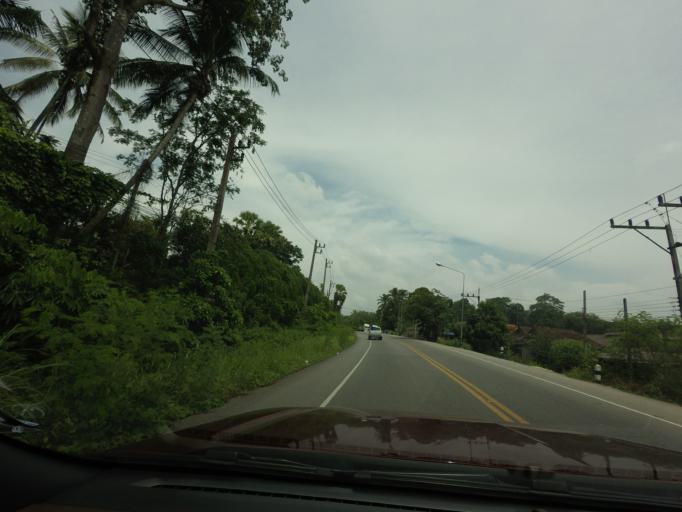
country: TH
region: Yala
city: Yala
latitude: 6.6040
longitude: 101.3030
